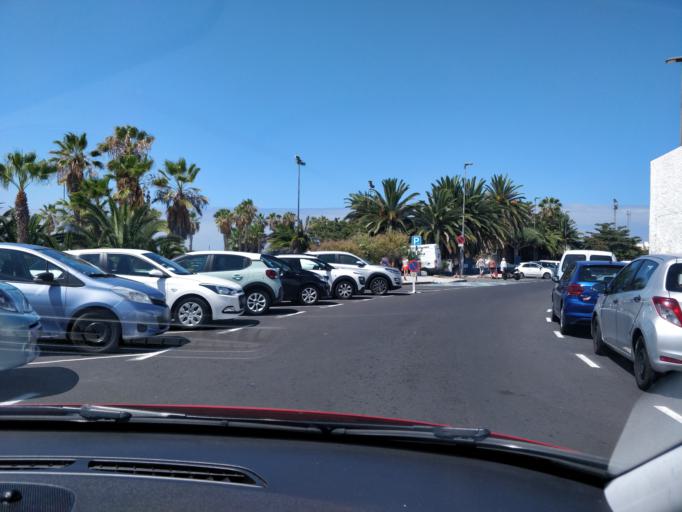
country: ES
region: Canary Islands
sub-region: Provincia de Santa Cruz de Tenerife
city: Puerto de la Cruz
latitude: 28.4141
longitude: -16.5581
